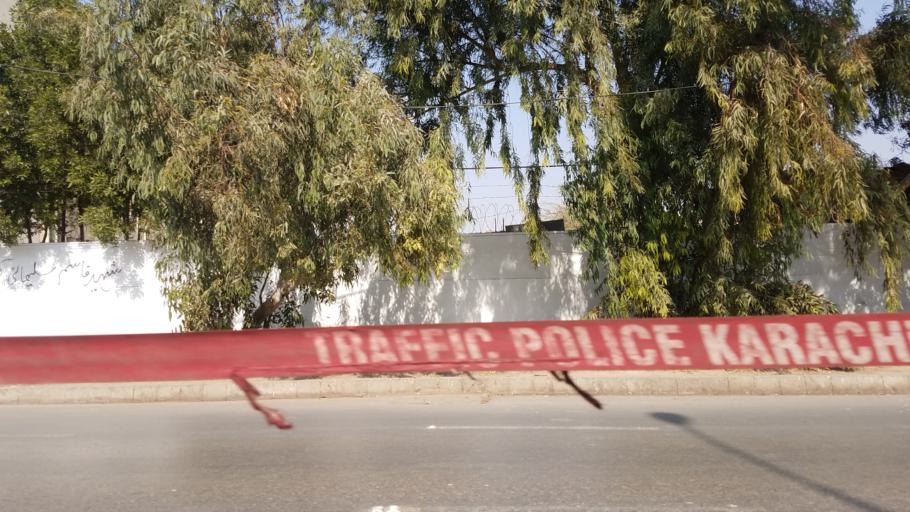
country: PK
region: Sindh
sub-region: Karachi District
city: Karachi
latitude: 24.8505
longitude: 67.0148
